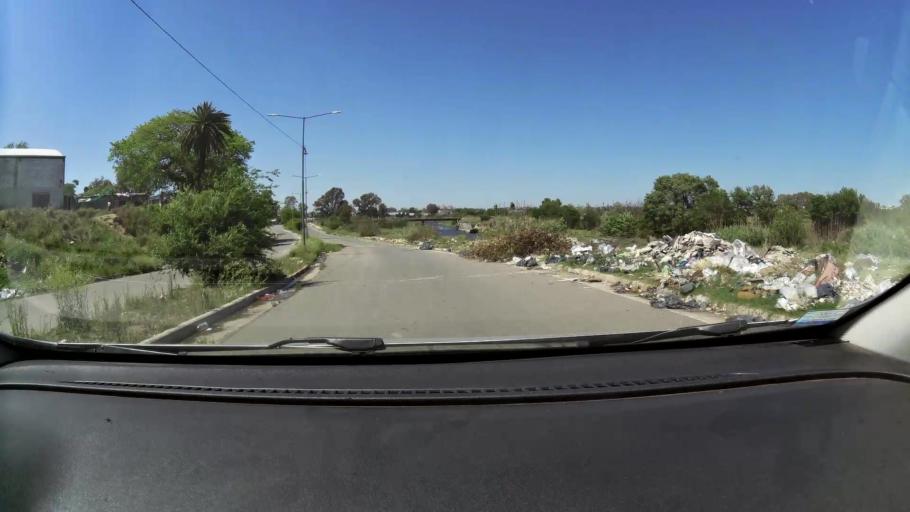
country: AR
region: Cordoba
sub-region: Departamento de Capital
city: Cordoba
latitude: -31.4085
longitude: -64.1415
